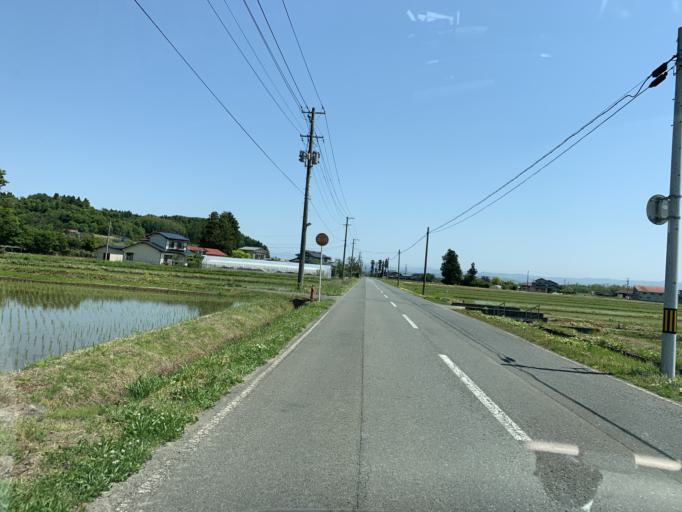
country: JP
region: Iwate
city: Mizusawa
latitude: 39.1655
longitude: 141.0815
